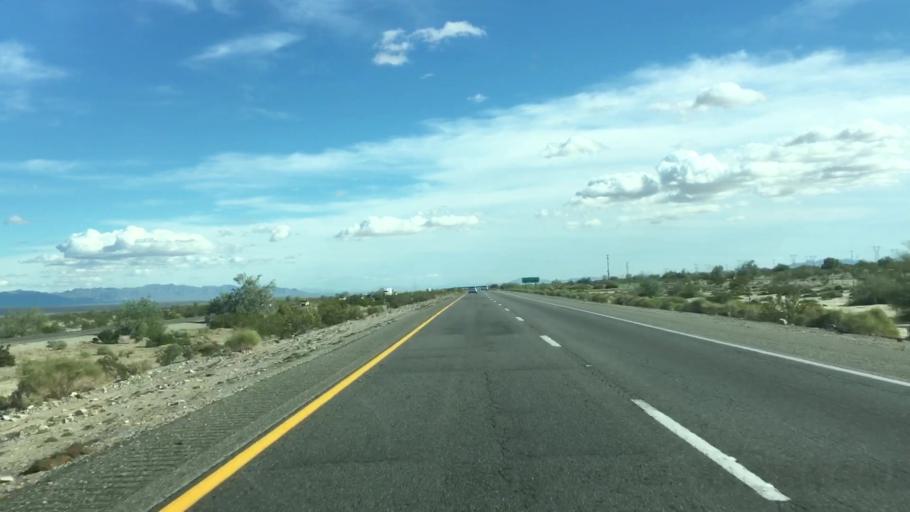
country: US
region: California
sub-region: Imperial County
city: Niland
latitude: 33.6882
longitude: -115.2635
